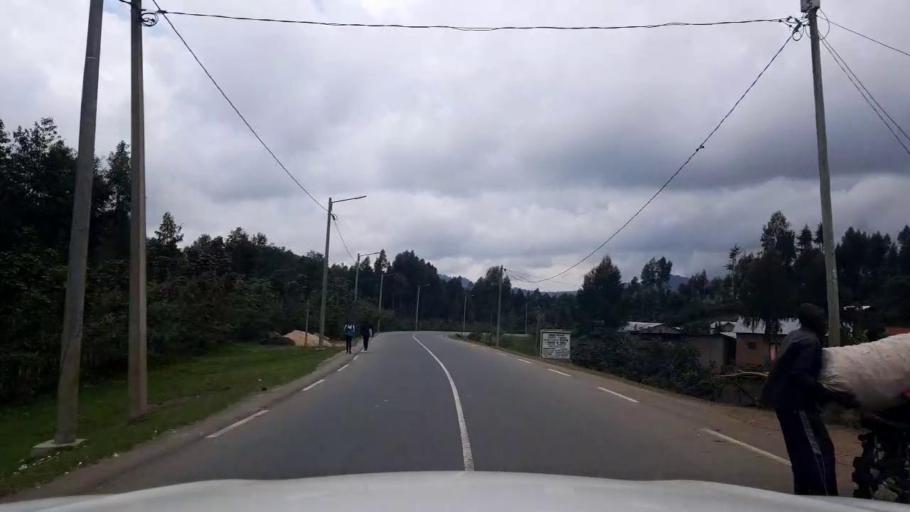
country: RW
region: Northern Province
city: Musanze
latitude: -1.6193
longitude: 29.5047
